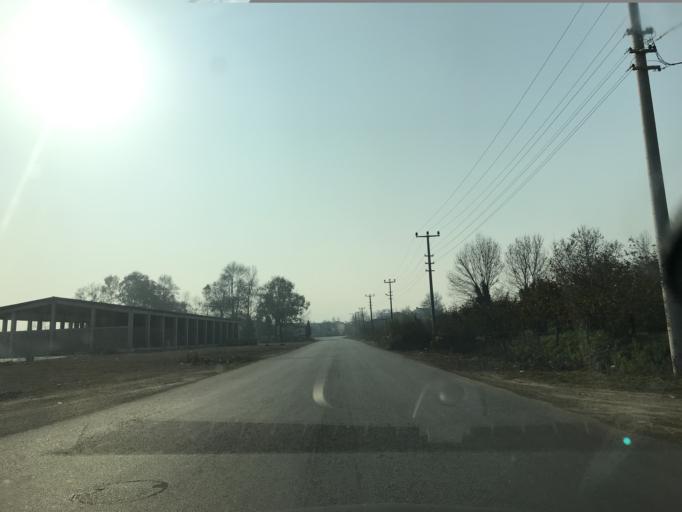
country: TR
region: Duzce
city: Cumayeri
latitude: 40.8869
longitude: 30.9522
